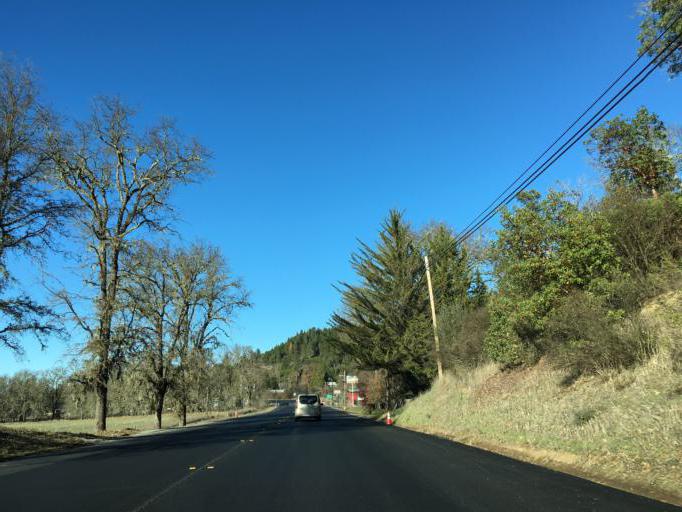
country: US
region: California
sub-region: Mendocino County
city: Laytonville
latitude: 39.6780
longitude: -123.4758
